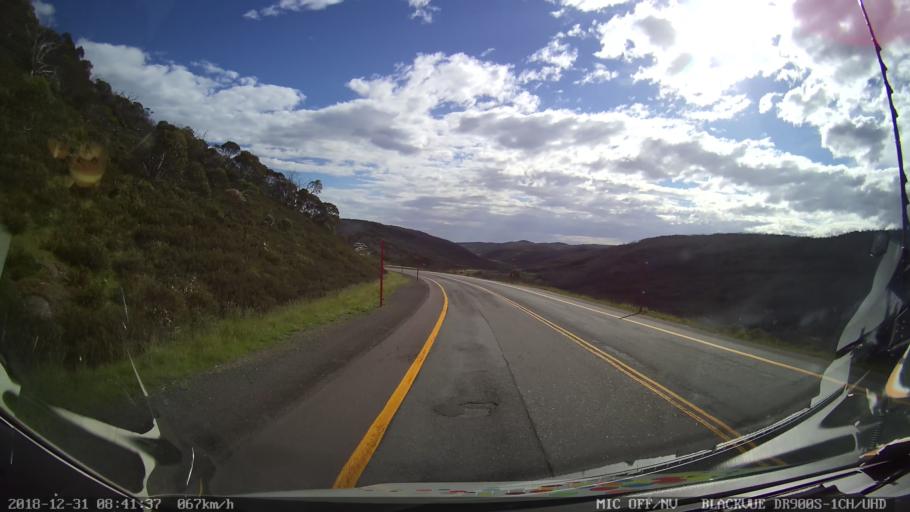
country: AU
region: New South Wales
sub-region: Snowy River
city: Jindabyne
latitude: -36.3973
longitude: 148.4239
